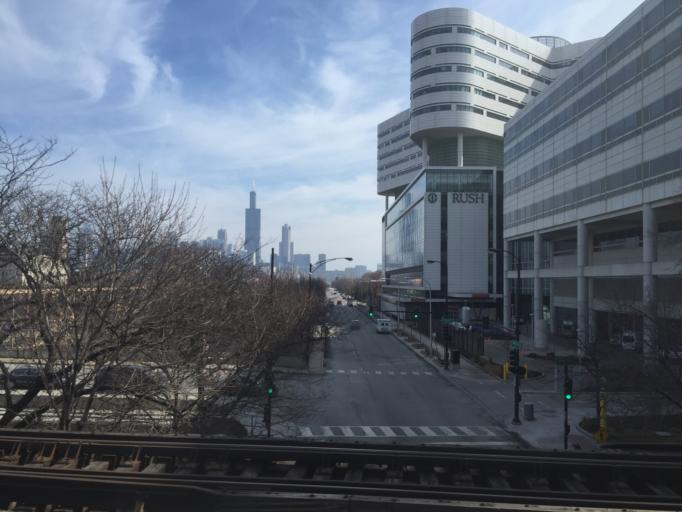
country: US
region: Illinois
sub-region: Cook County
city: Chicago
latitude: 41.8752
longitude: -87.6698
